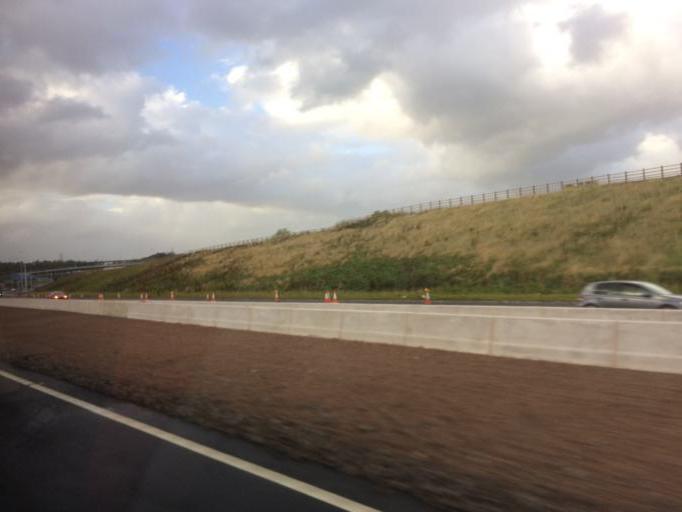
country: GB
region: Scotland
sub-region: South Lanarkshire
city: Uddingston
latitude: 55.8468
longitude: -4.0730
